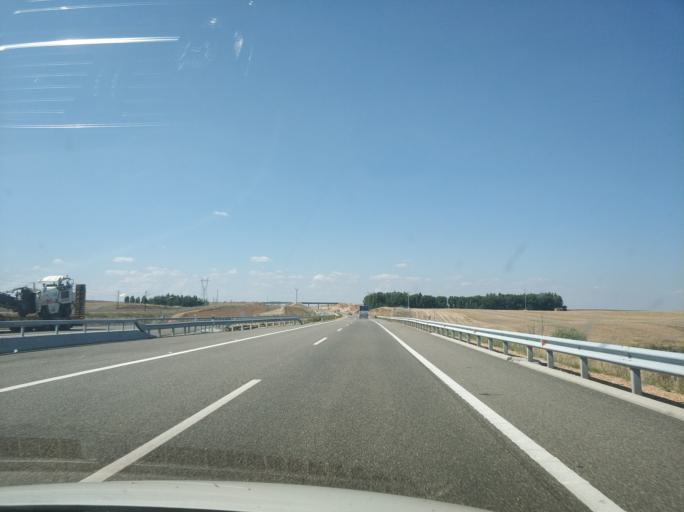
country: ES
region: Castille and Leon
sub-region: Provincia de Zamora
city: Montamarta
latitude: 41.6484
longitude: -5.7939
